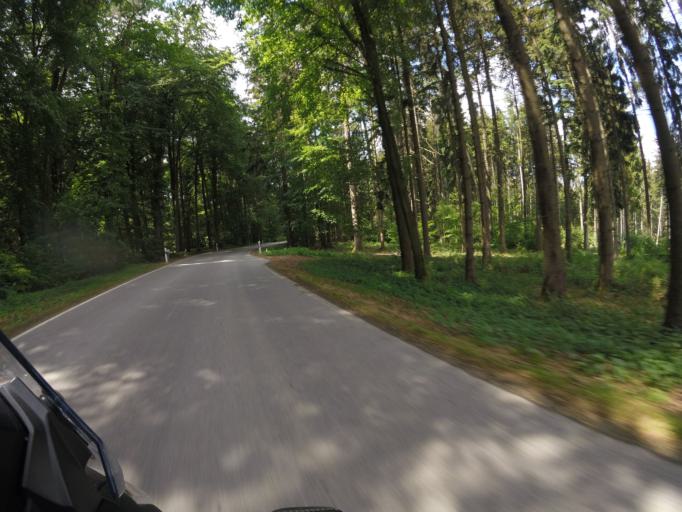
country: DE
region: Bavaria
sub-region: Lower Bavaria
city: Kirchdorf
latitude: 48.7337
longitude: 11.9375
